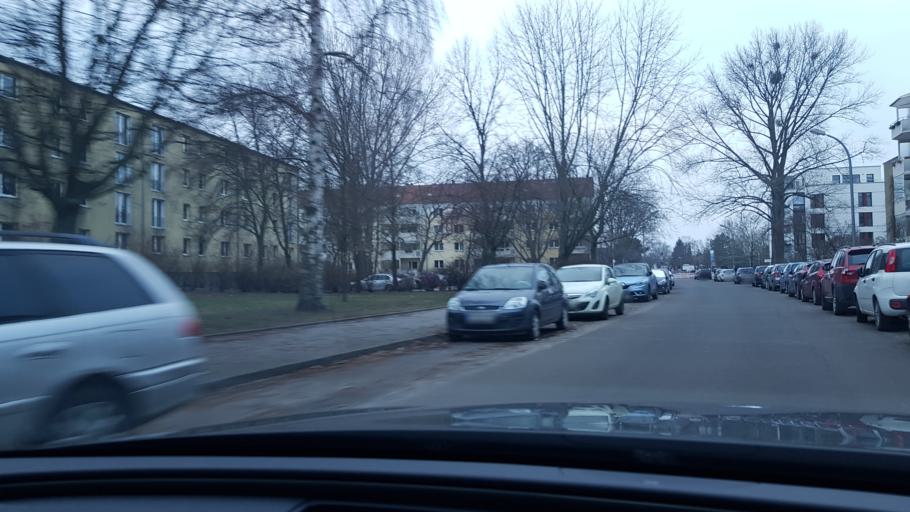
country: DE
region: Berlin
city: Grunau
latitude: 52.4274
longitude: 13.5930
